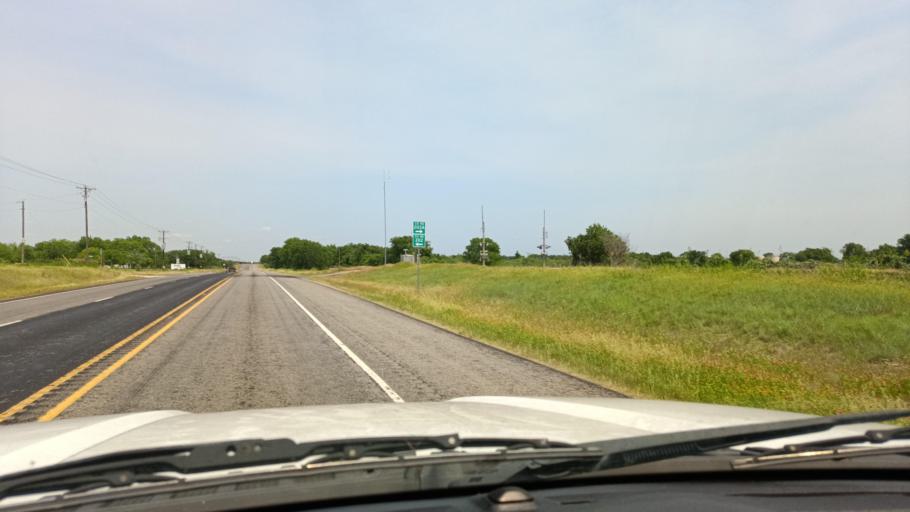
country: US
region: Texas
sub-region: Milam County
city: Cameron
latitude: 30.8489
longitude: -97.0516
